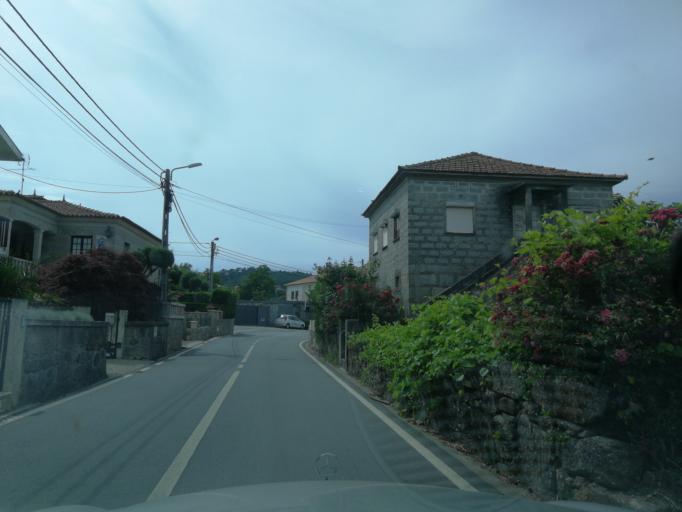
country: PT
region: Braga
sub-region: Vila Nova de Famalicao
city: Calendario
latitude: 41.4104
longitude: -8.5385
